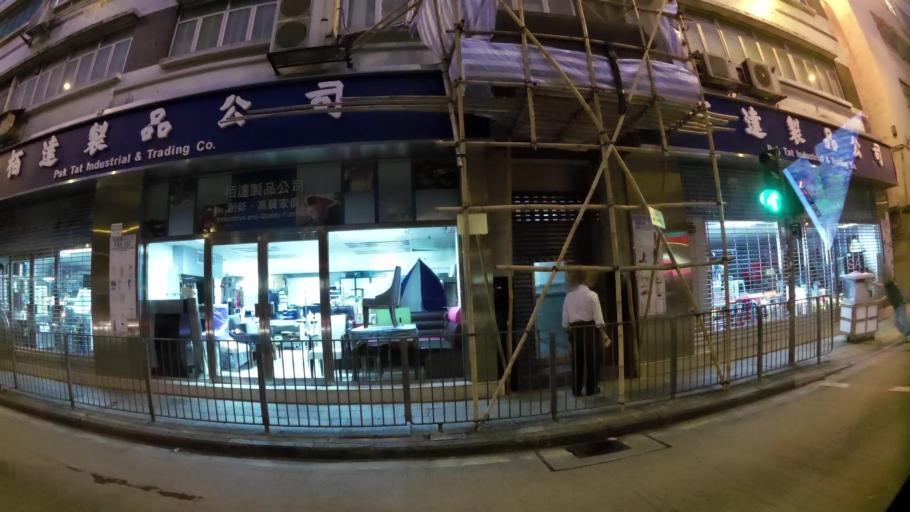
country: HK
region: Sham Shui Po
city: Sham Shui Po
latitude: 22.3221
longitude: 114.1656
